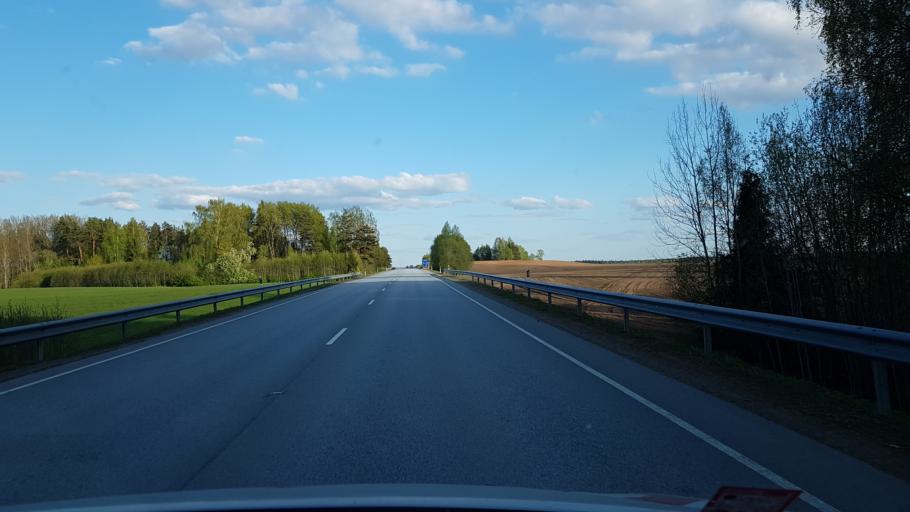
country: EE
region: Vorumaa
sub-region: Voru linn
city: Voru
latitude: 57.8969
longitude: 26.8427
